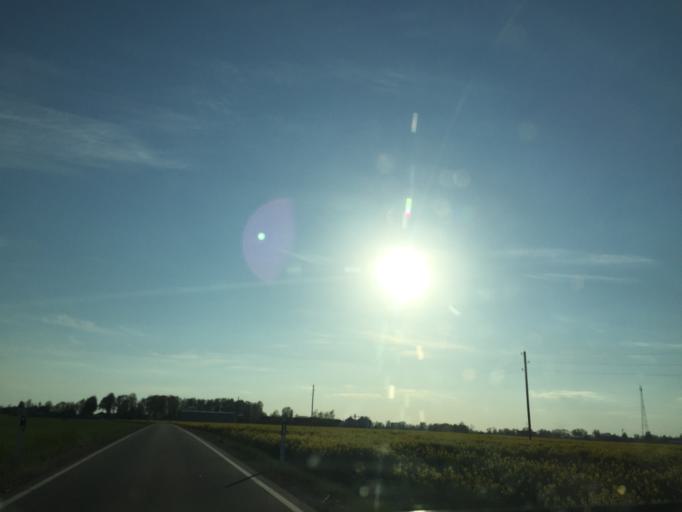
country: LV
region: Bauskas Rajons
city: Bauska
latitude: 56.3107
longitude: 24.2712
